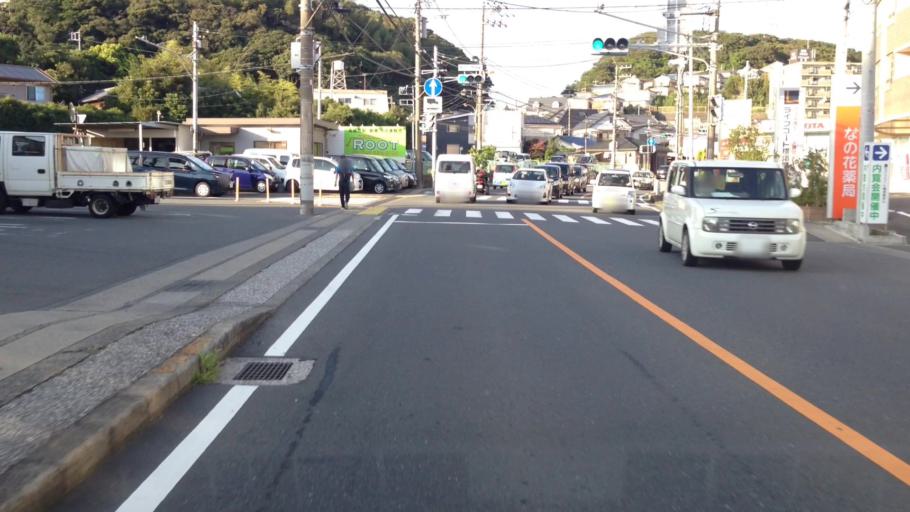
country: JP
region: Kanagawa
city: Yokosuka
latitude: 35.2294
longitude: 139.6523
